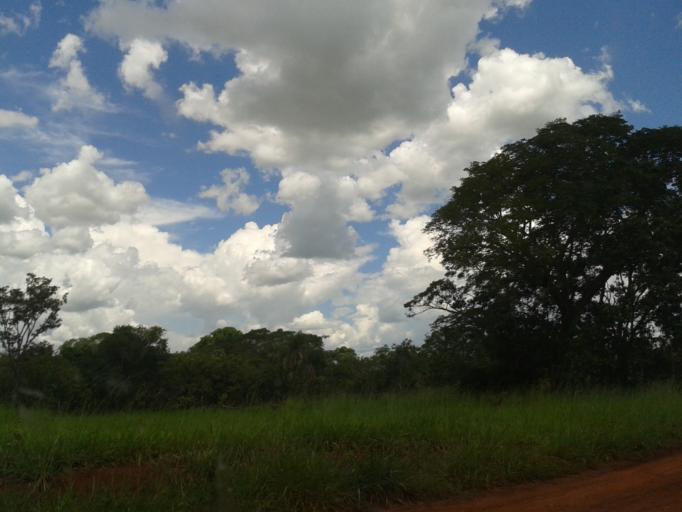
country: BR
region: Minas Gerais
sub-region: Capinopolis
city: Capinopolis
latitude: -18.7883
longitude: -49.8030
